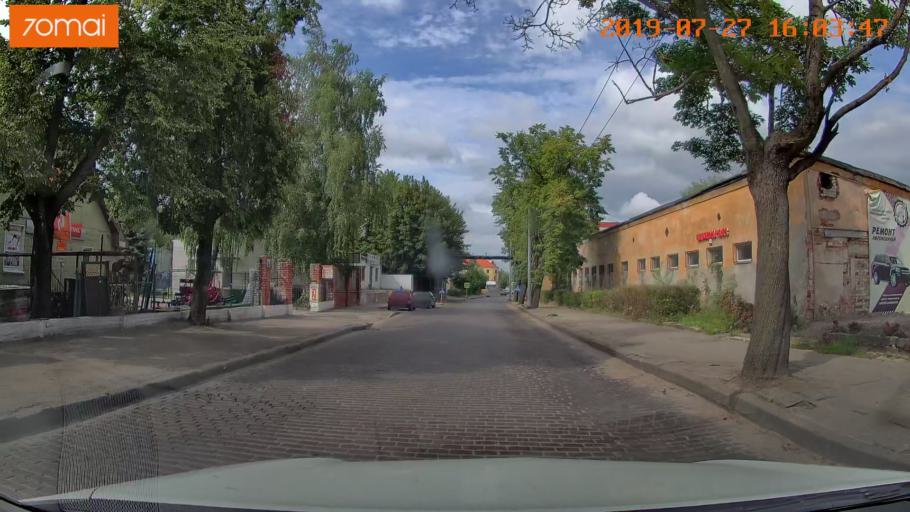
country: RU
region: Kaliningrad
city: Chernyakhovsk
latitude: 54.6337
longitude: 21.8031
